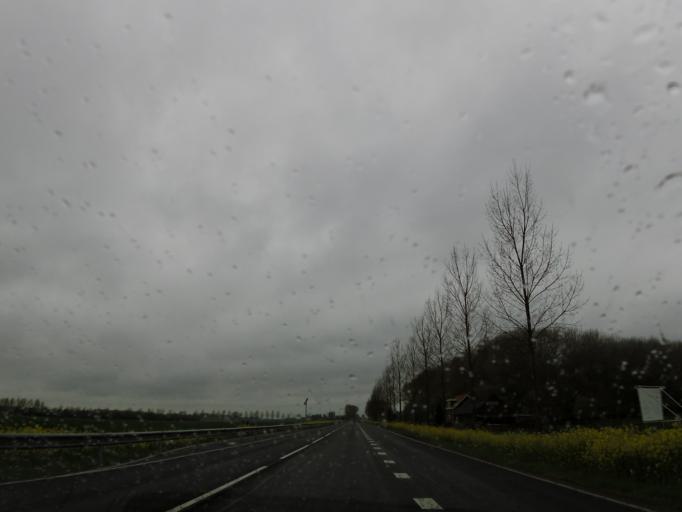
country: NL
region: Gelderland
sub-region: Gemeente Culemborg
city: Culemborg
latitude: 51.9337
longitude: 5.1785
